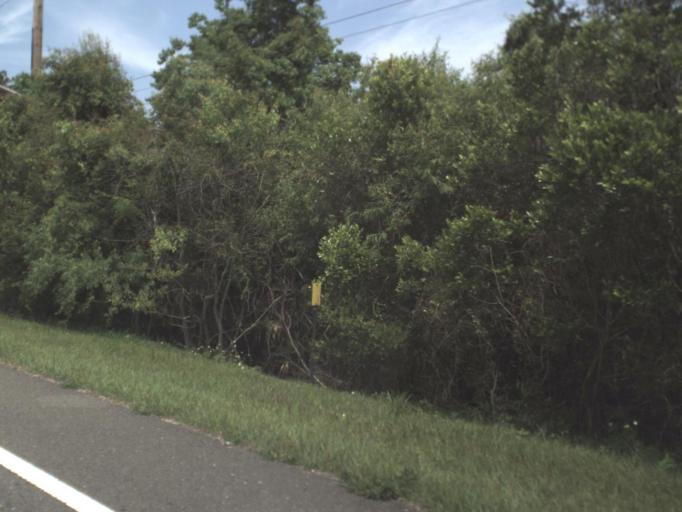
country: US
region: Florida
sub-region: Duval County
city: Jacksonville
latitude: 30.4273
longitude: -81.6457
